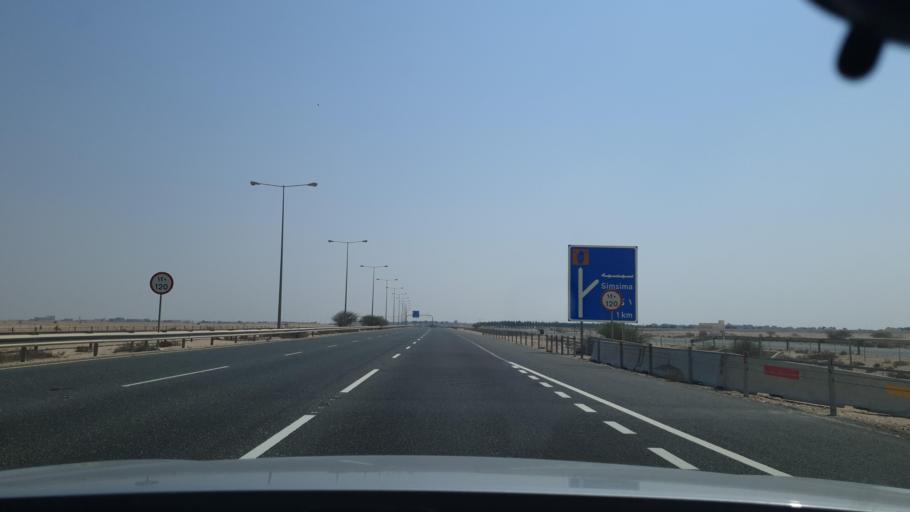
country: QA
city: Al Ghuwayriyah
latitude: 25.7960
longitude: 51.3869
